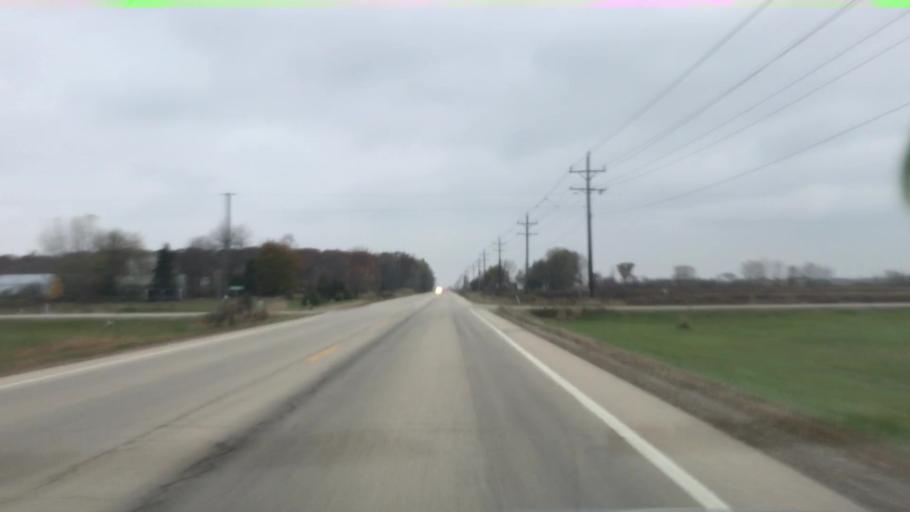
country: US
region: Wisconsin
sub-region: Outagamie County
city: Seymour
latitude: 44.4866
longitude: -88.2911
